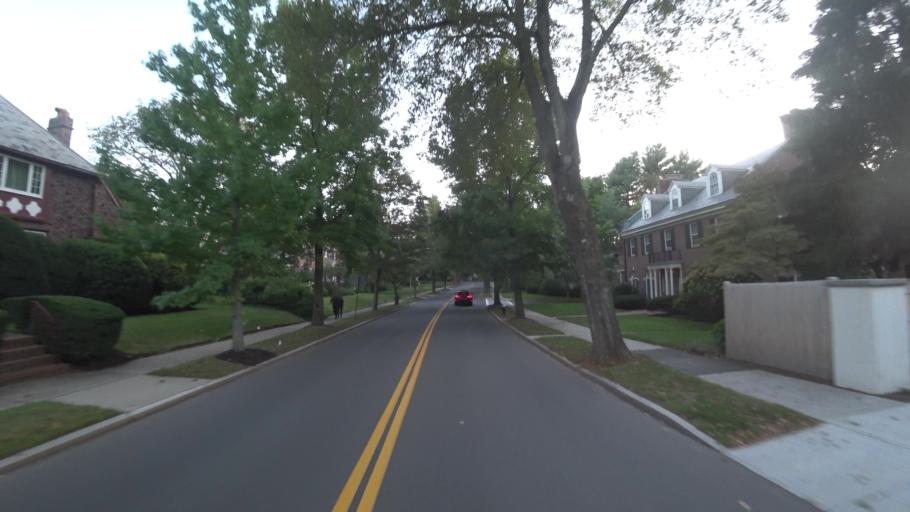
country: US
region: Massachusetts
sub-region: Norfolk County
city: Brookline
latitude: 42.3323
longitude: -71.1483
